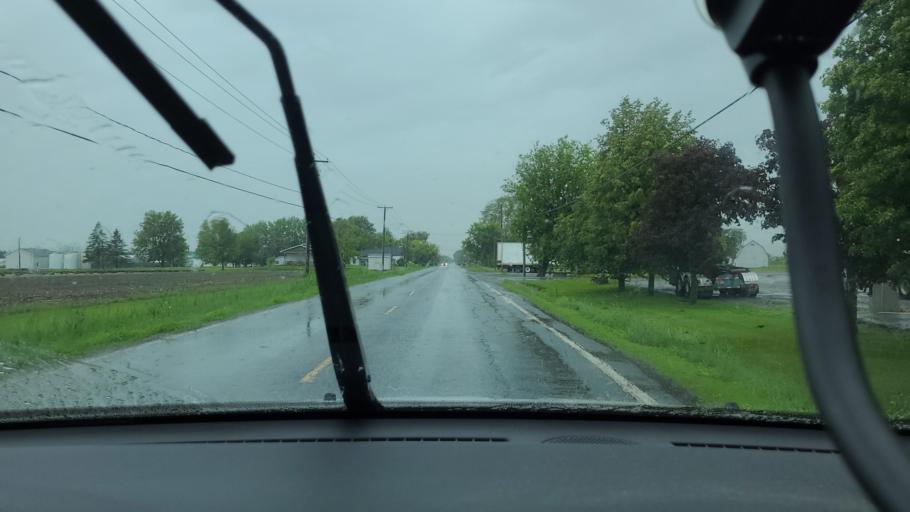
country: CA
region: Quebec
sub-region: Monteregie
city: Saint-Hyacinthe
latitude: 45.6167
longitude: -73.0215
